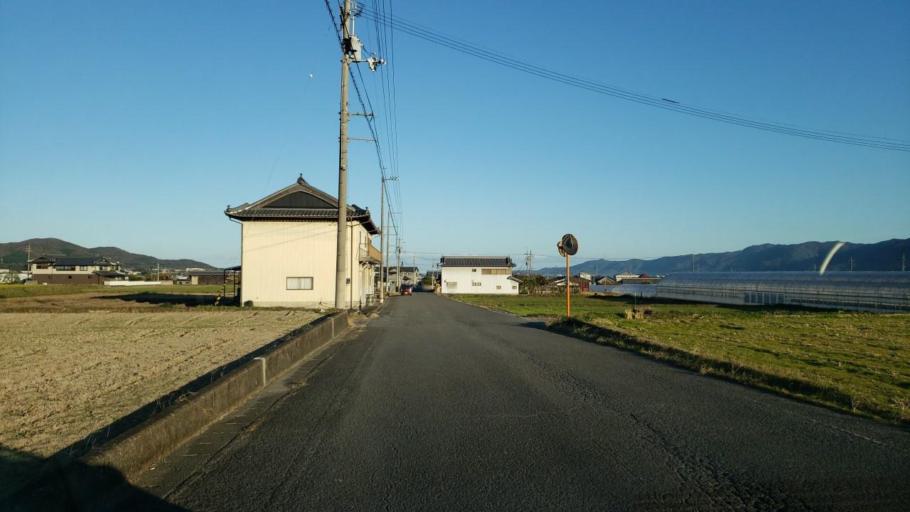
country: JP
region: Tokushima
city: Kamojimacho-jogejima
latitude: 34.0914
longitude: 134.2511
